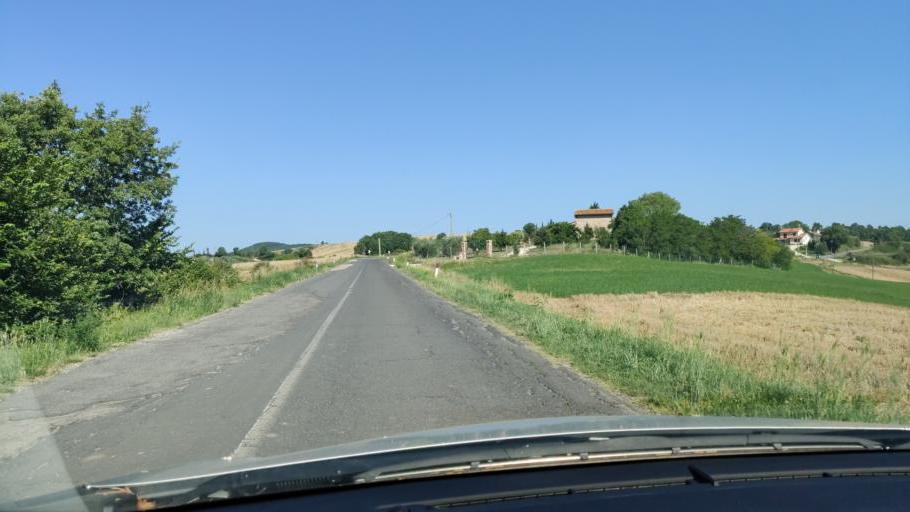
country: IT
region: Umbria
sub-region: Provincia di Terni
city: Avigliano Umbro
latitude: 42.6725
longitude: 12.4423
